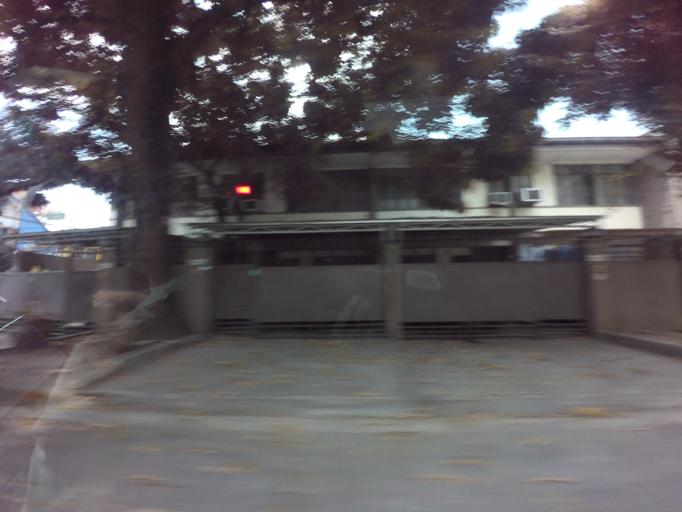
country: PH
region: Metro Manila
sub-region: Mandaluyong
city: Mandaluyong City
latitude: 14.5732
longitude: 121.0251
